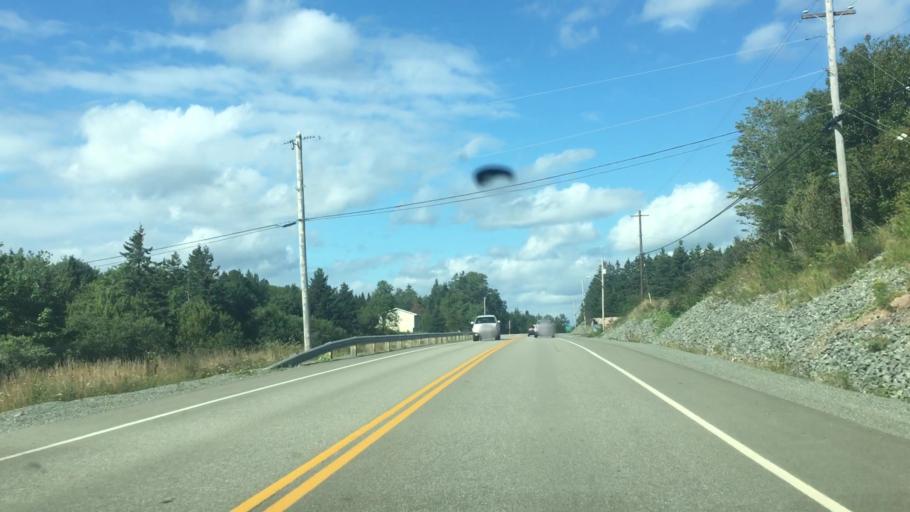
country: CA
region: Nova Scotia
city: Princeville
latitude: 45.6875
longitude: -60.7535
